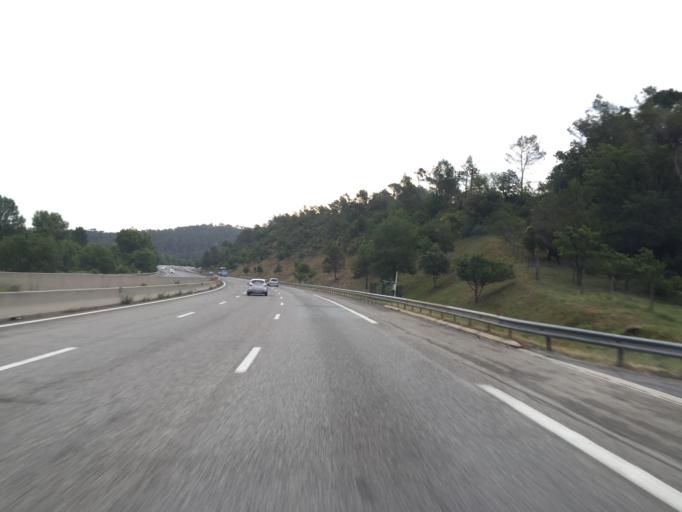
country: FR
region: Provence-Alpes-Cote d'Azur
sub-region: Departement du Var
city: Camps-la-Source
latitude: 43.4177
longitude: 6.1087
